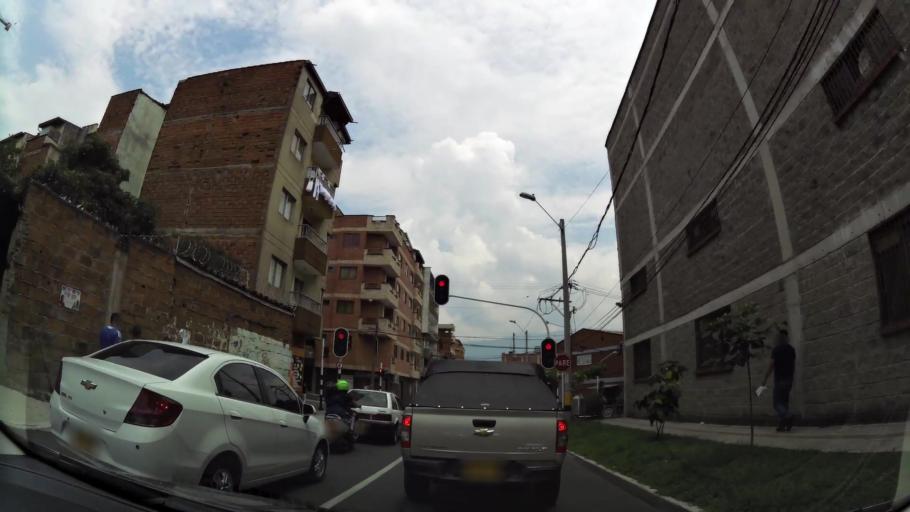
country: CO
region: Antioquia
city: Itagui
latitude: 6.1698
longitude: -75.6080
